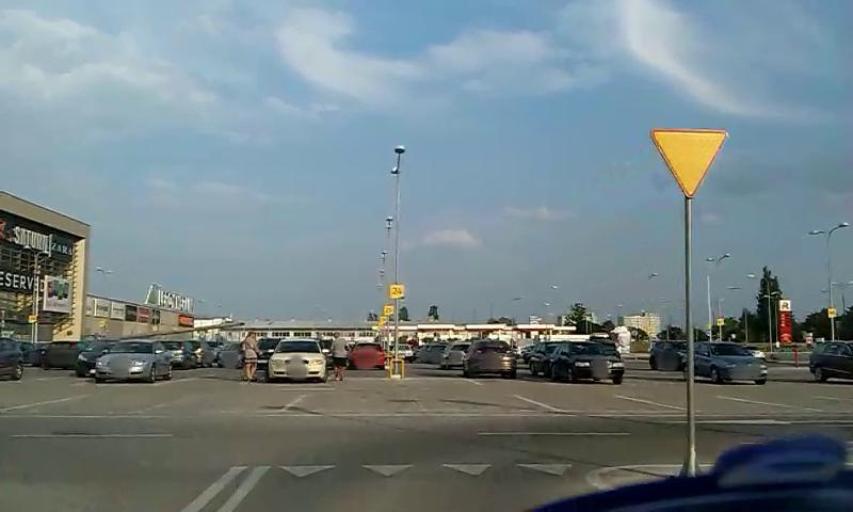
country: PL
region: Lublin Voivodeship
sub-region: Powiat lubelski
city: Jakubowice Murowane
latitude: 51.2311
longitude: 22.6140
